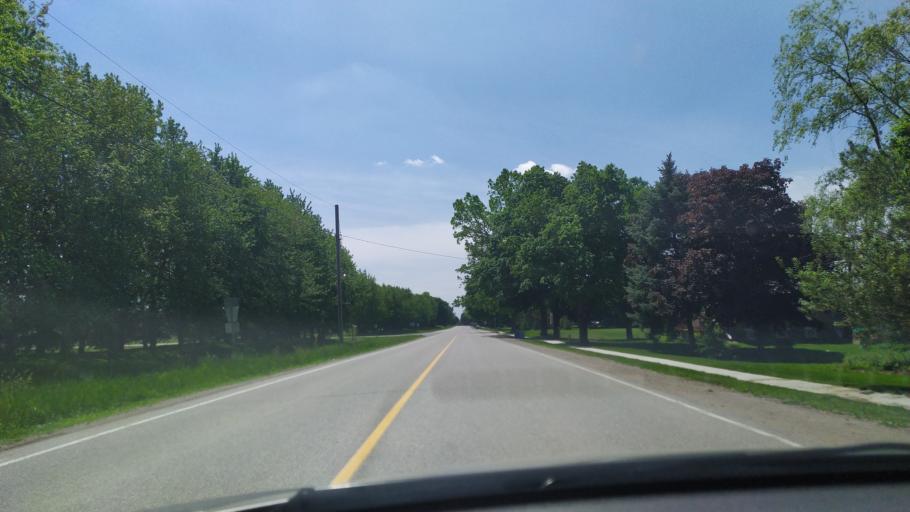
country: CA
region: Ontario
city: Ingersoll
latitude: 42.9885
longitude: -80.9534
